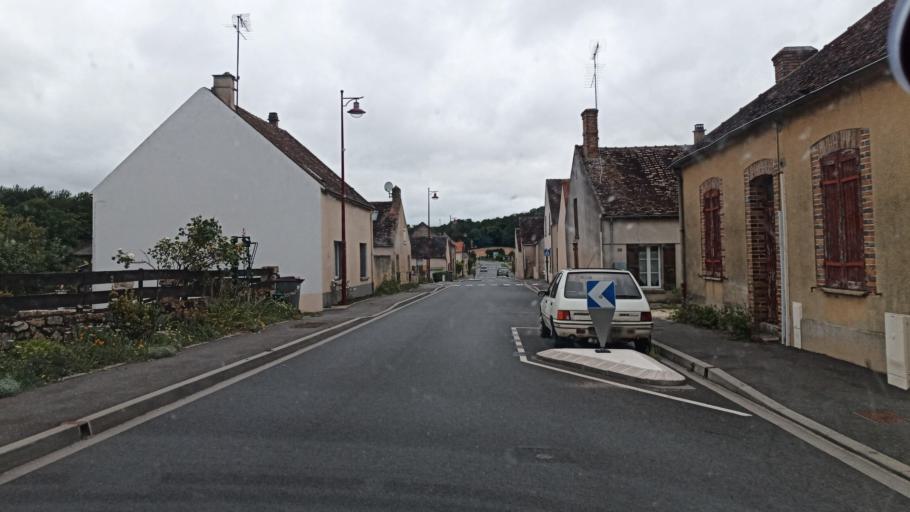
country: FR
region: Ile-de-France
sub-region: Departement de Seine-et-Marne
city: Voulx
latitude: 48.2862
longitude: 2.9597
